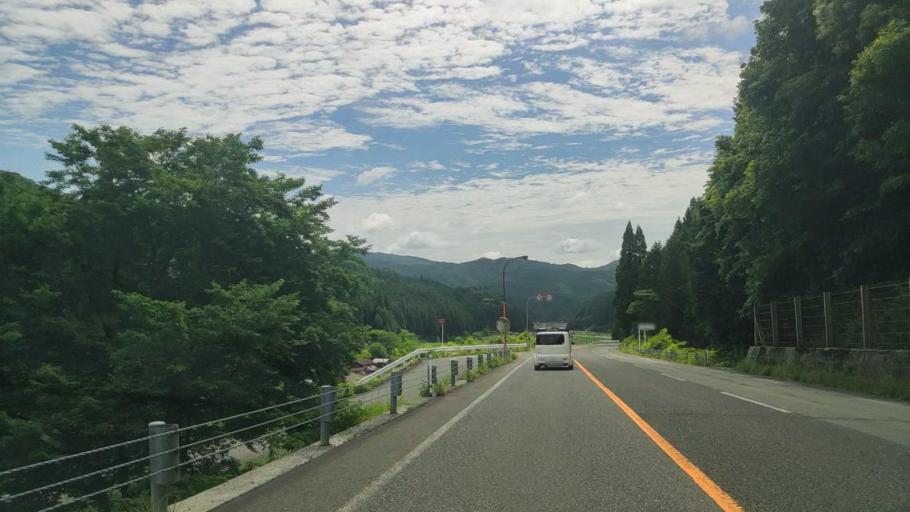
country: JP
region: Okayama
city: Niimi
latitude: 35.1797
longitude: 133.5539
